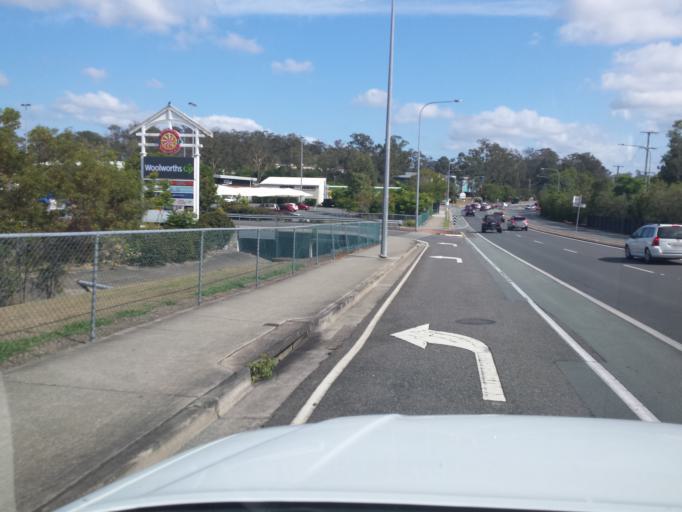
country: AU
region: Queensland
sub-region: Brisbane
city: Bridegman Downs
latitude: -27.3594
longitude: 152.9706
